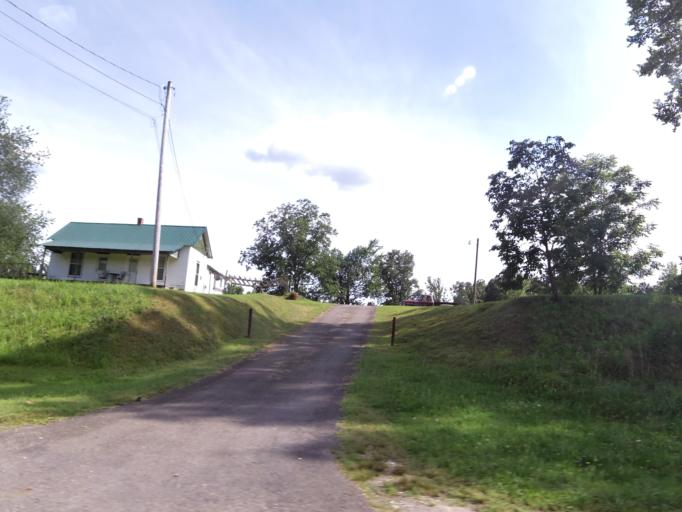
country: US
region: Tennessee
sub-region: Carroll County
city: Bruceton
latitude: 36.0380
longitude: -88.3014
